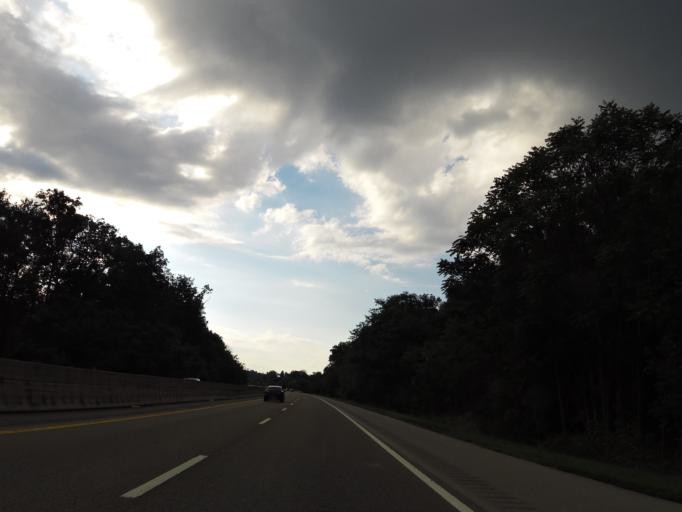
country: US
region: Tennessee
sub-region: Blount County
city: Louisville
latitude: 35.8579
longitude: -84.0251
